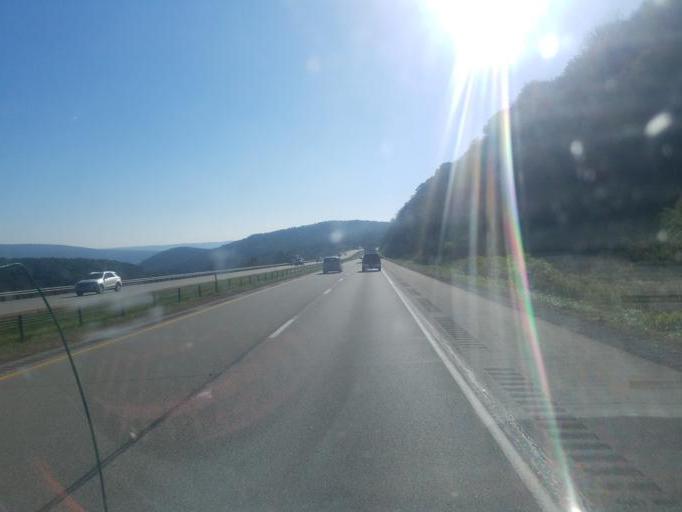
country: US
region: Pennsylvania
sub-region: Cambria County
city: Gallitzin
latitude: 40.4720
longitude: -78.4927
